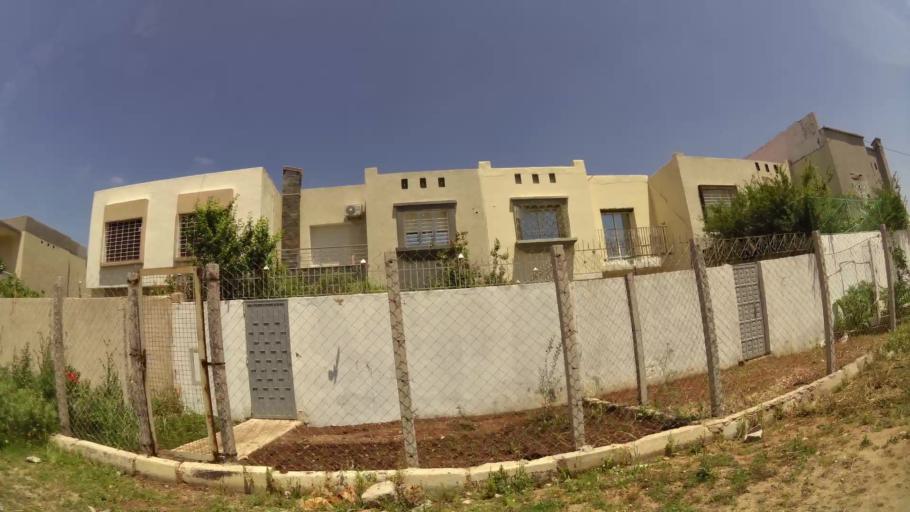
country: MA
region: Fes-Boulemane
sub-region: Fes
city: Fes
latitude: 34.0377
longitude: -5.0432
